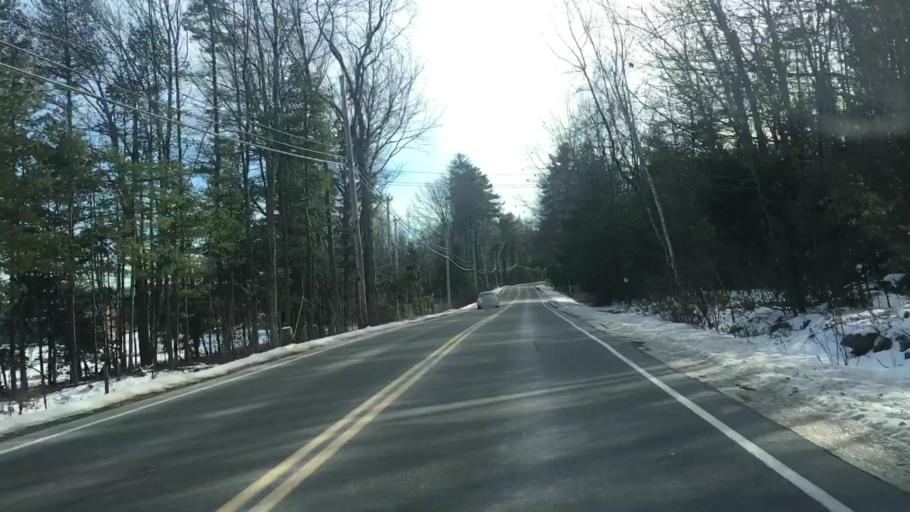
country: US
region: Maine
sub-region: Cumberland County
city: Westbrook
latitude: 43.7013
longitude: -70.3575
